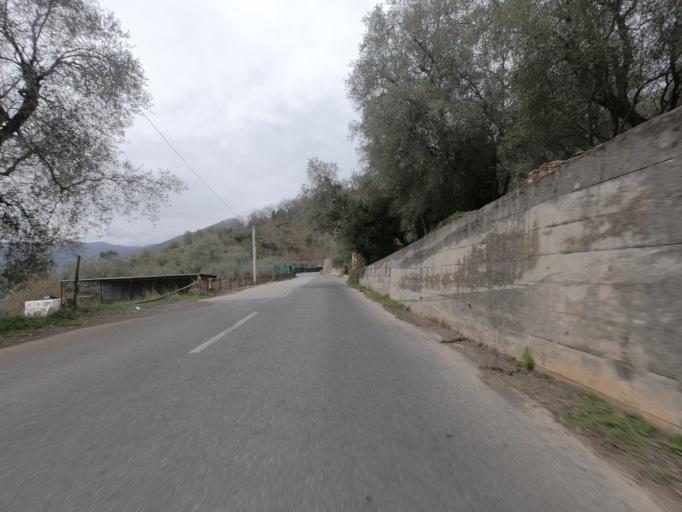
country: IT
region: Liguria
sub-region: Provincia di Savona
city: Casanova Lerrone
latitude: 44.0310
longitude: 8.0437
